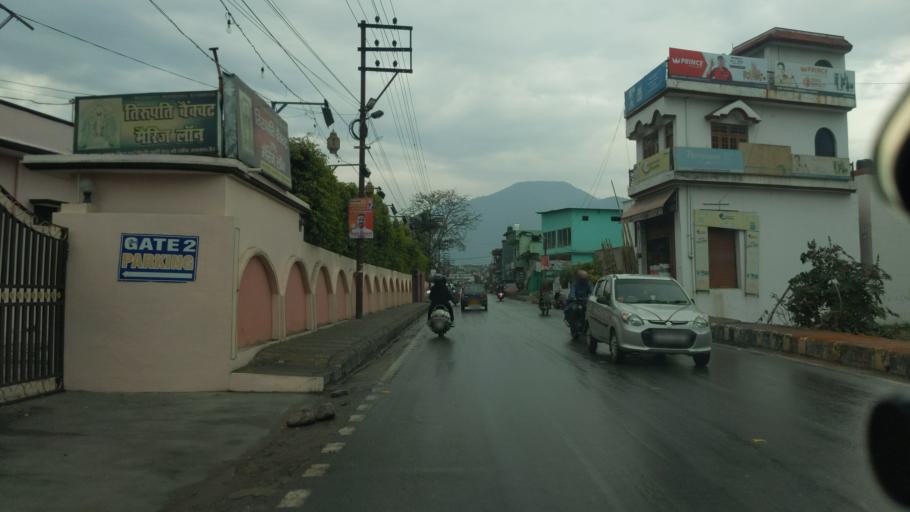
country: IN
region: Uttarakhand
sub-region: Naini Tal
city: Haldwani
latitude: 29.2422
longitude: 79.5295
